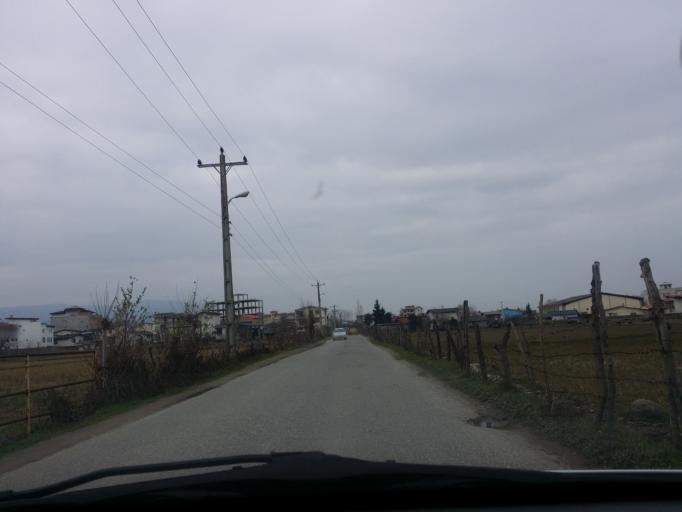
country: IR
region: Mazandaran
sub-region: Nowshahr
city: Nowshahr
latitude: 36.6433
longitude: 51.4839
